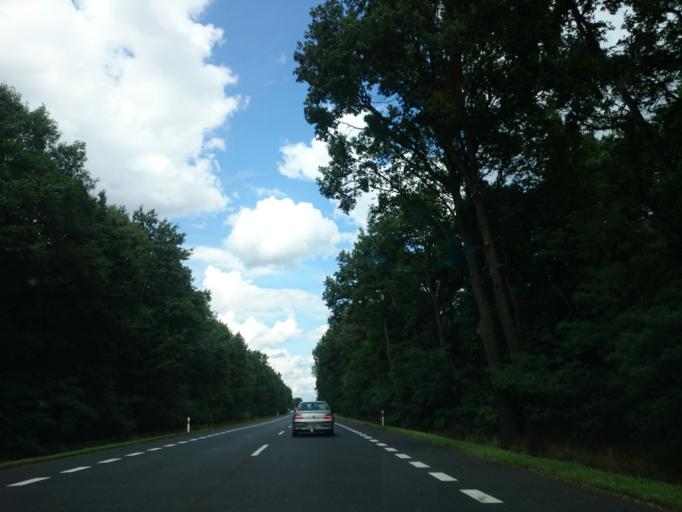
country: PL
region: Lubusz
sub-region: Powiat nowosolski
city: Nowe Miasteczko
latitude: 51.7136
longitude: 15.7295
